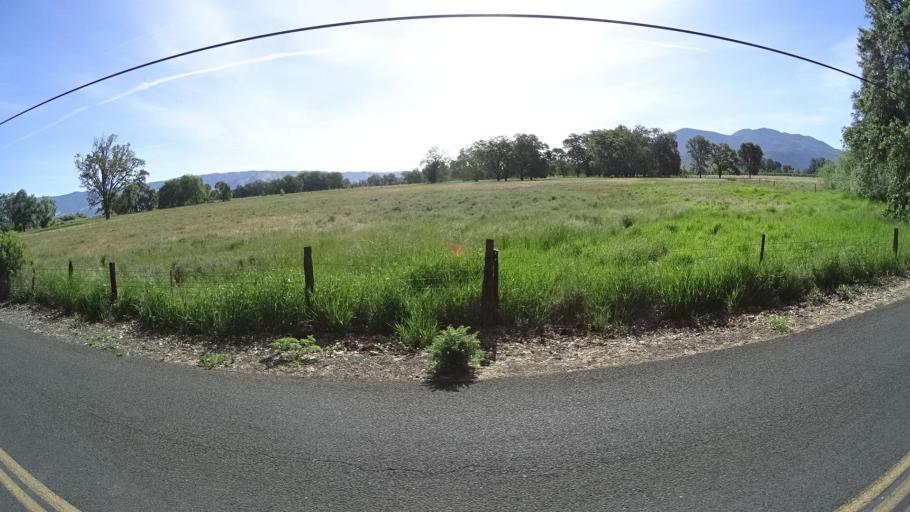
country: US
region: California
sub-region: Lake County
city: Kelseyville
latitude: 39.0230
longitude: -122.8475
